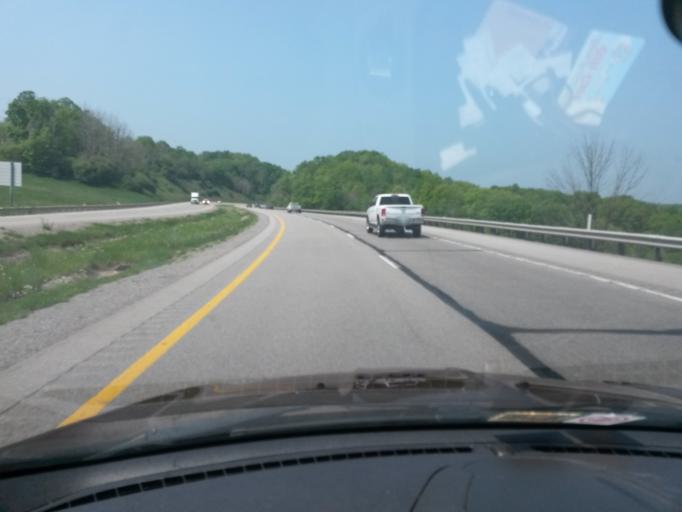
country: US
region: West Virginia
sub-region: Lewis County
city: Weston
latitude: 38.9146
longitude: -80.5804
